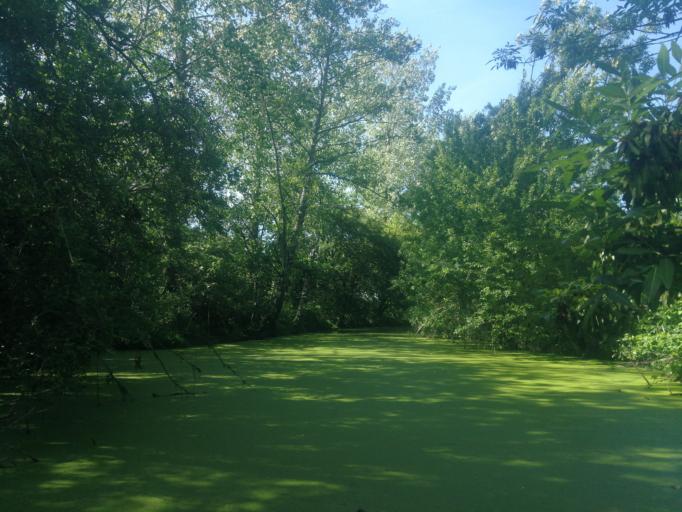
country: FR
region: Poitou-Charentes
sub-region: Departement de la Charente-Maritime
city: Marans
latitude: 46.3653
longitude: -0.9645
